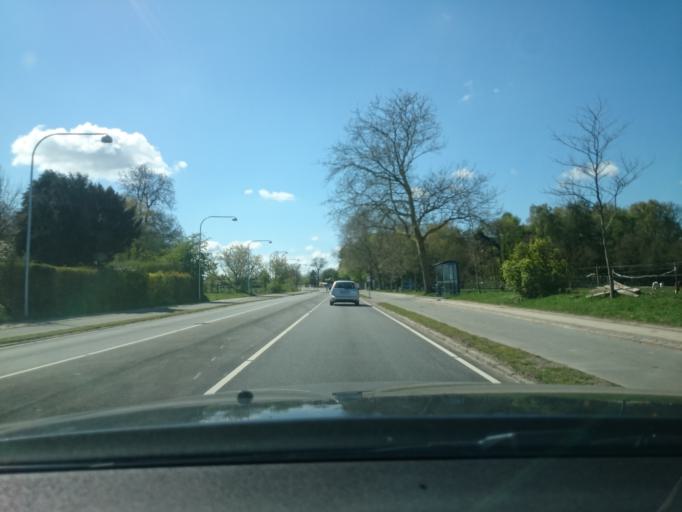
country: DK
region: Capital Region
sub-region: Lyngby-Tarbaek Kommune
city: Kongens Lyngby
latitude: 55.7794
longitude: 12.5386
